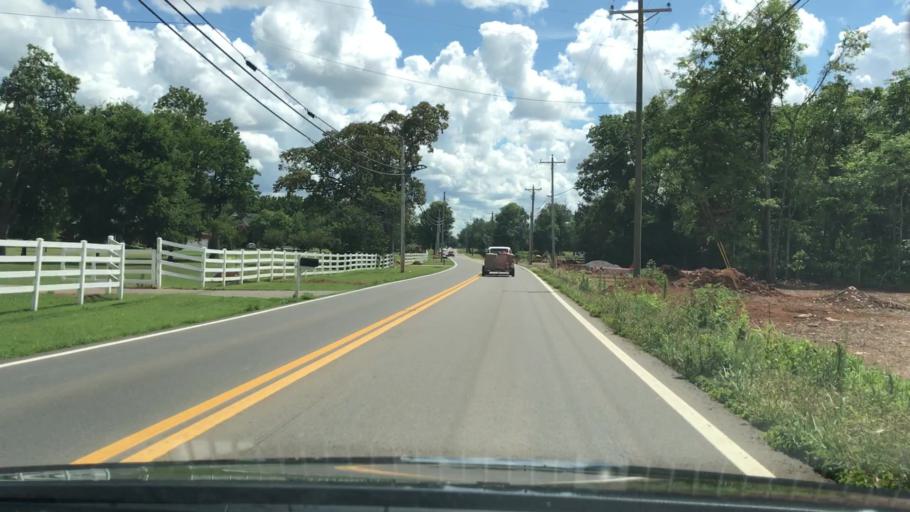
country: US
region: Tennessee
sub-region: Rutherford County
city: Murfreesboro
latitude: 35.8418
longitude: -86.5087
